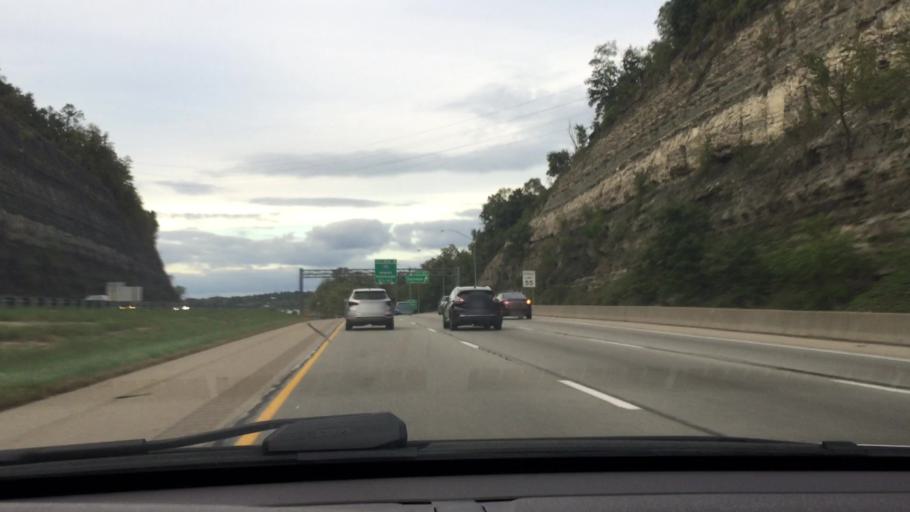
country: US
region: Pennsylvania
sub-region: Allegheny County
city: Heidelberg
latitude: 40.3908
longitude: -80.0995
